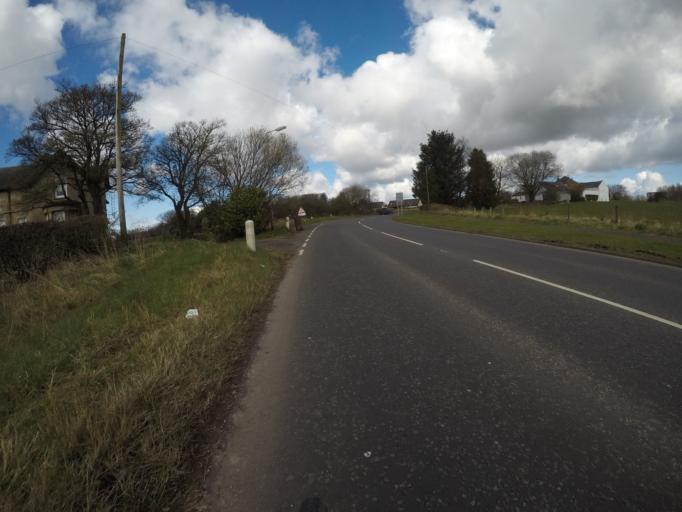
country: GB
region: Scotland
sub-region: North Ayrshire
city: Beith
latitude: 55.7452
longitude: -4.6287
